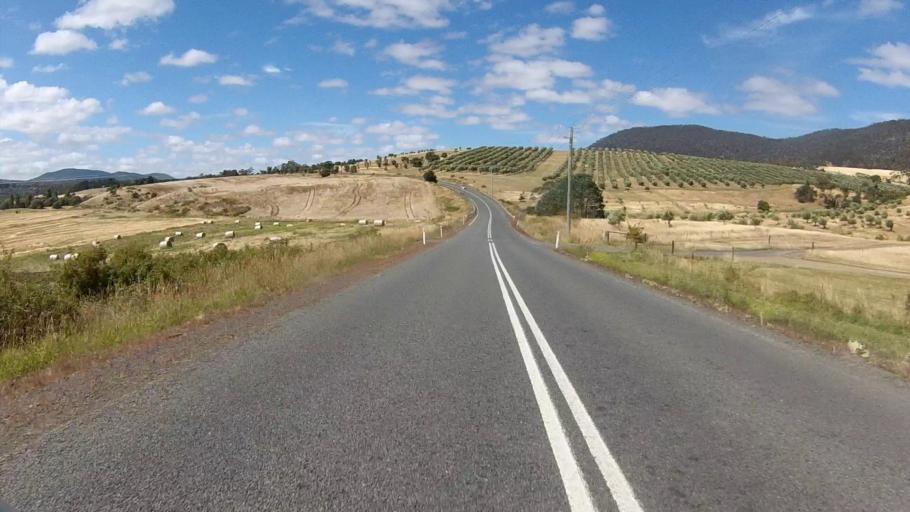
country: AU
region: Tasmania
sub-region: Brighton
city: Old Beach
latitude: -42.6020
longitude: 147.4167
